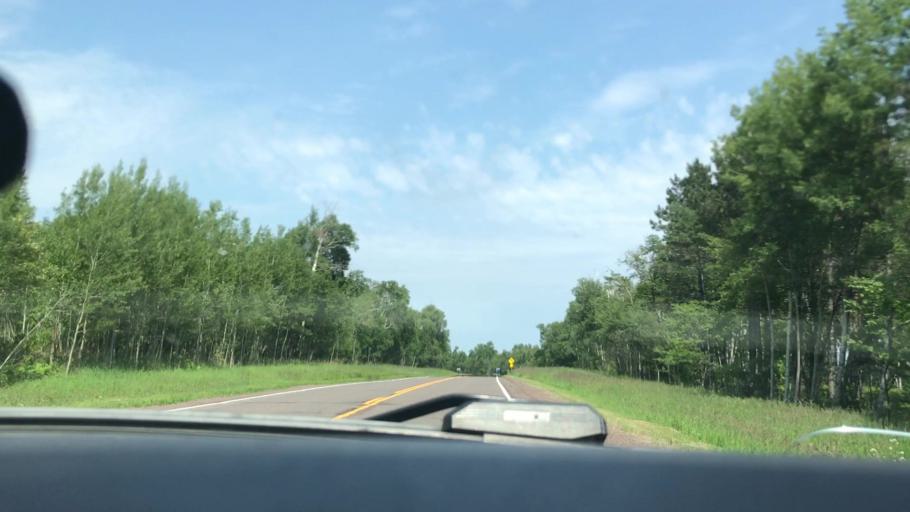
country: US
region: Minnesota
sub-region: Lake County
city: Silver Bay
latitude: 47.4928
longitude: -90.9783
